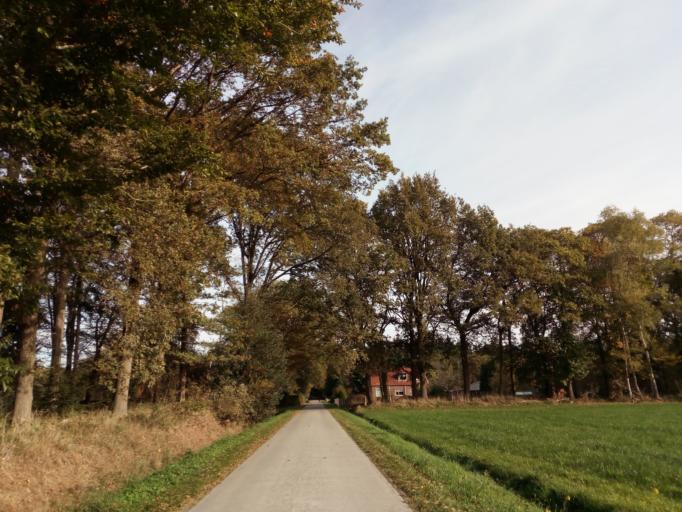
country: NL
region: Overijssel
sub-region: Gemeente Steenwijkerland
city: Tuk
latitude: 52.8217
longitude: 6.0948
